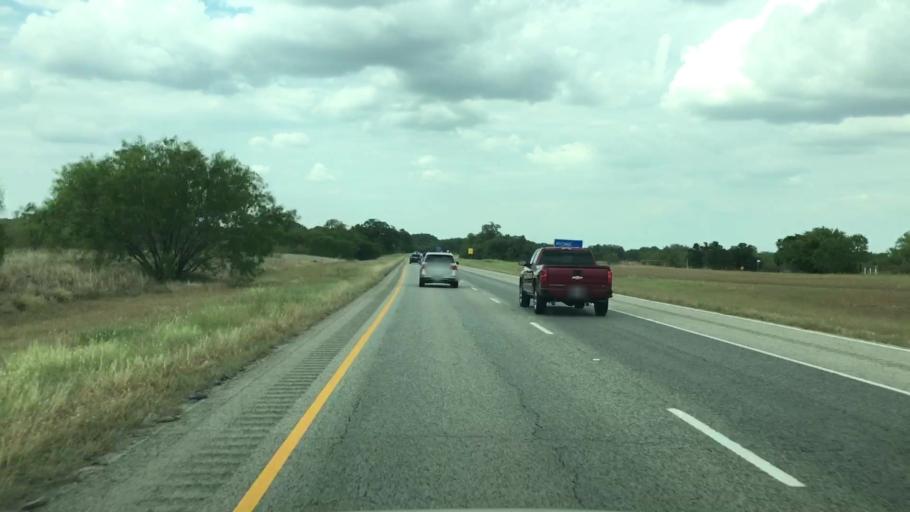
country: US
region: Texas
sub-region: Atascosa County
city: Pleasanton
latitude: 29.0273
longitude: -98.4315
